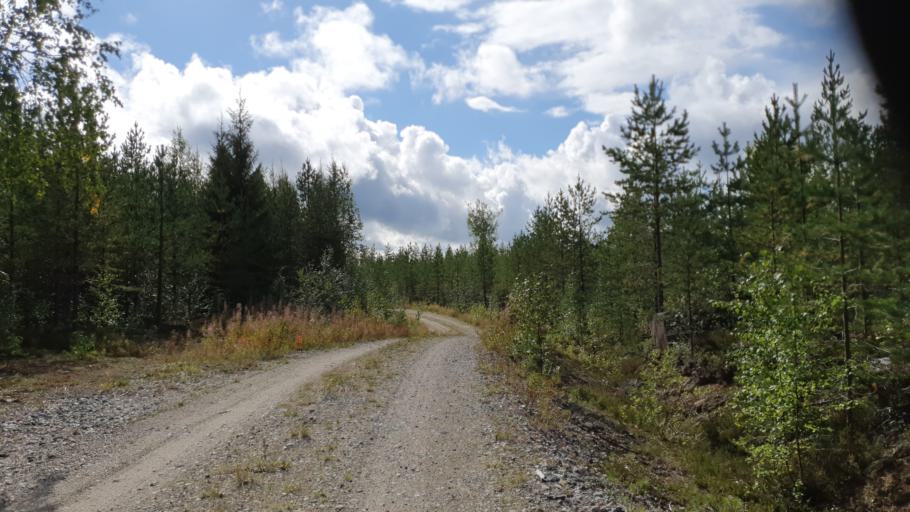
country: FI
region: Kainuu
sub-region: Kehys-Kainuu
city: Kuhmo
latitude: 64.1468
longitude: 29.3876
